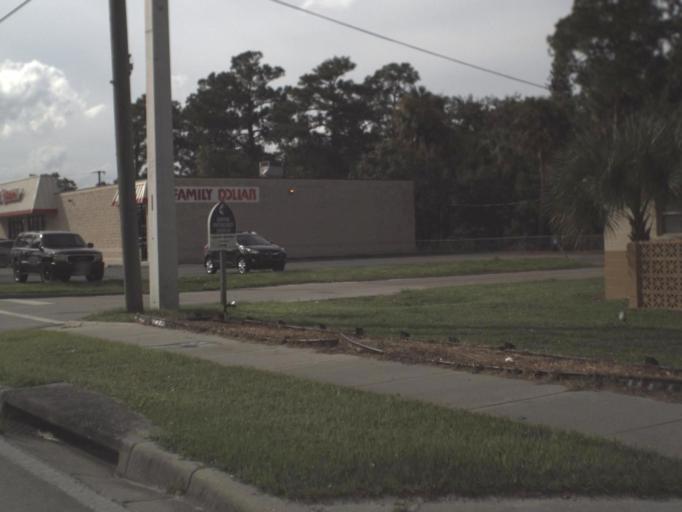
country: US
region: Florida
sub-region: Hendry County
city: LaBelle
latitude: 26.7617
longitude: -81.4414
